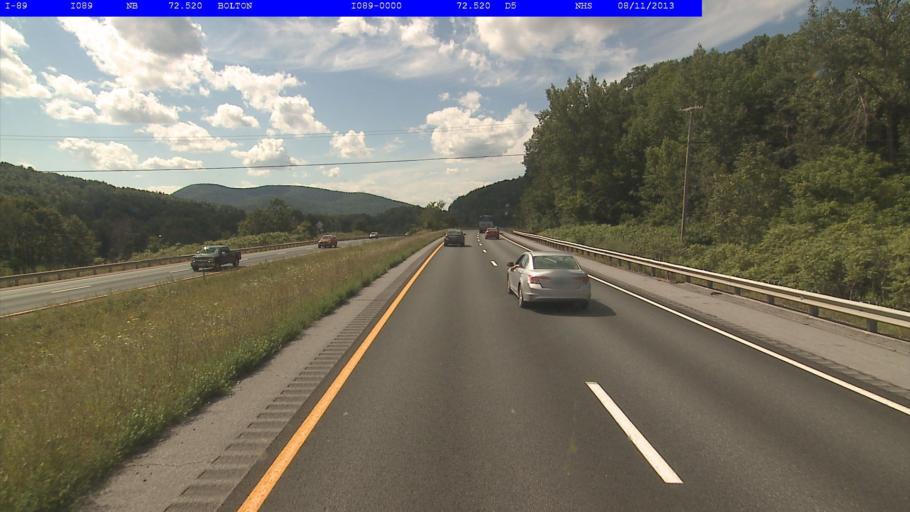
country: US
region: Vermont
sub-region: Chittenden County
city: Jericho
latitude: 44.3808
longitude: -72.9163
